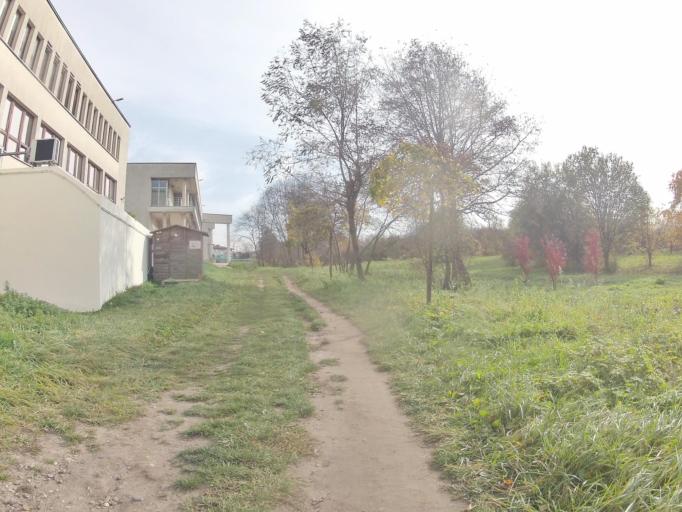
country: PL
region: Lesser Poland Voivodeship
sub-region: Krakow
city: Sidzina
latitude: 50.0258
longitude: 19.9000
